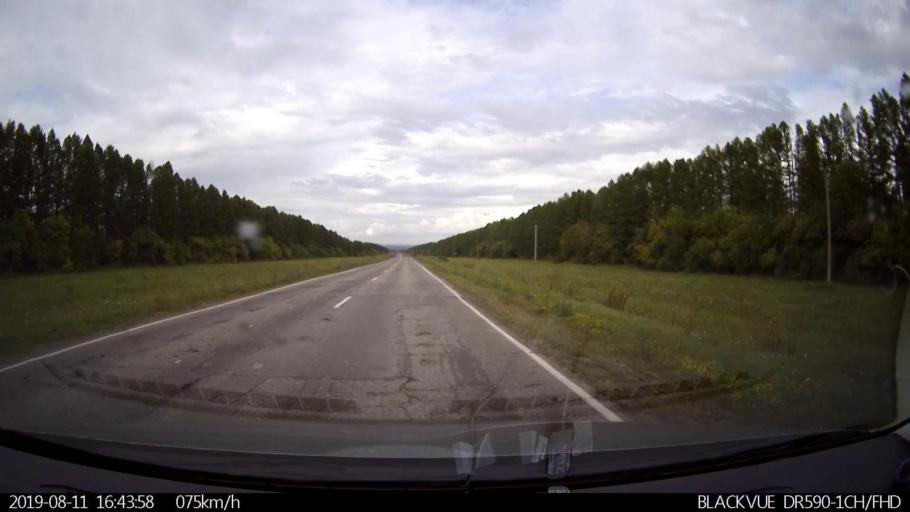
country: RU
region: Ulyanovsk
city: Mayna
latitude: 54.1744
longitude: 47.6771
